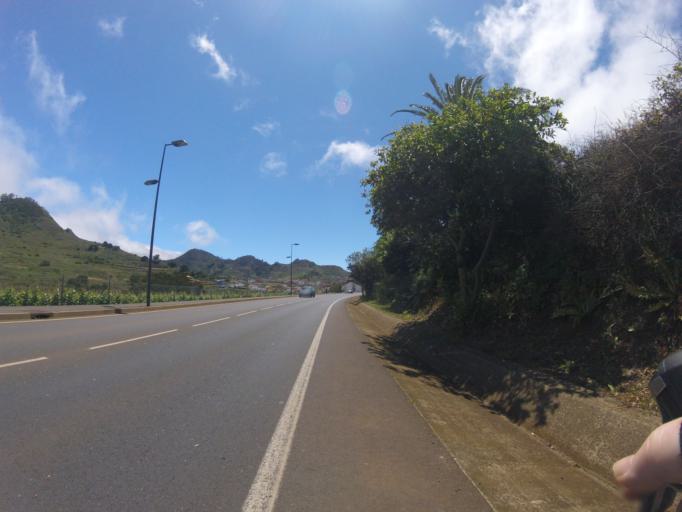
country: ES
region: Canary Islands
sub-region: Provincia de Santa Cruz de Tenerife
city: Tegueste
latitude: 28.5192
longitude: -16.3276
